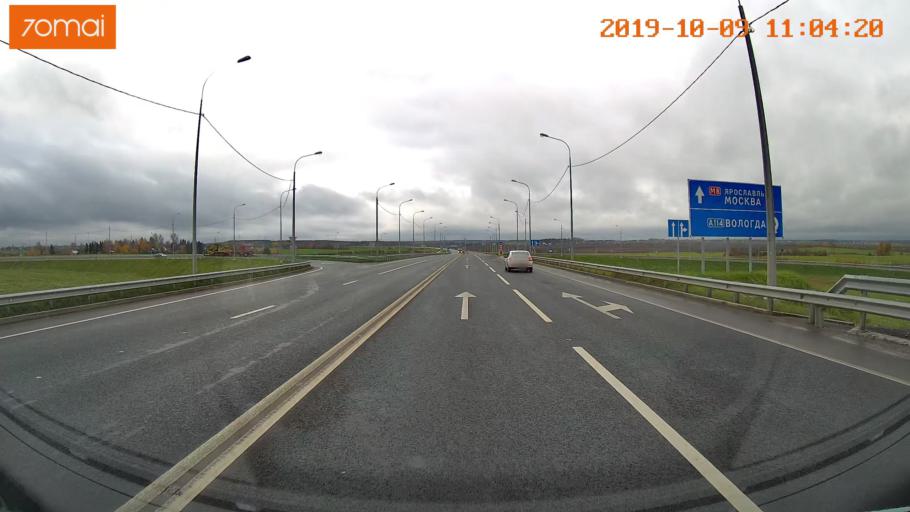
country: RU
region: Vologda
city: Vologda
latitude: 59.2130
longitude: 39.7684
